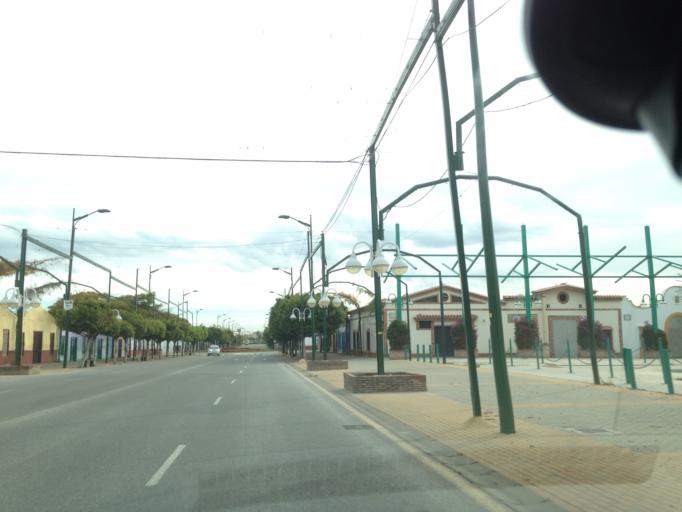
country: ES
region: Andalusia
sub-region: Provincia de Malaga
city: Malaga
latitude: 36.7045
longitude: -4.4640
